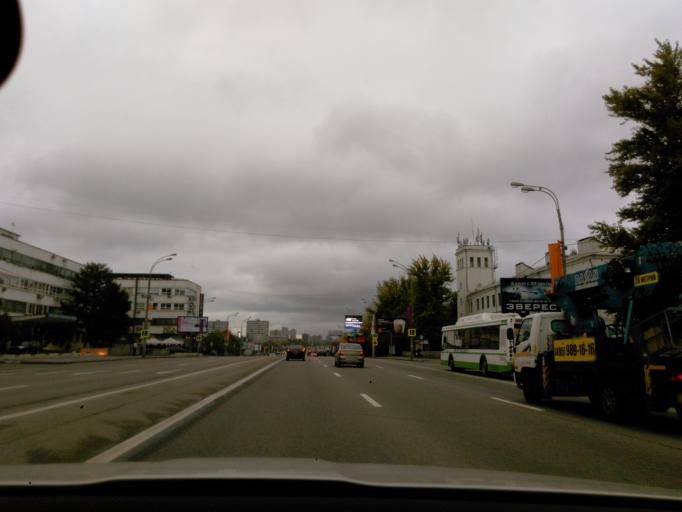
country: RU
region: Moscow
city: Strogino
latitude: 55.8293
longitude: 37.4116
